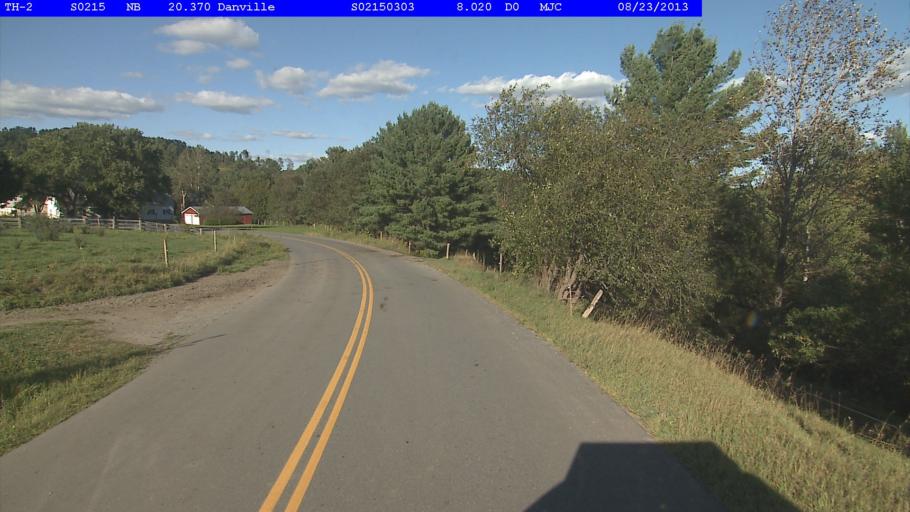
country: US
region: Vermont
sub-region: Caledonia County
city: St Johnsbury
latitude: 44.4580
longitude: -72.1003
